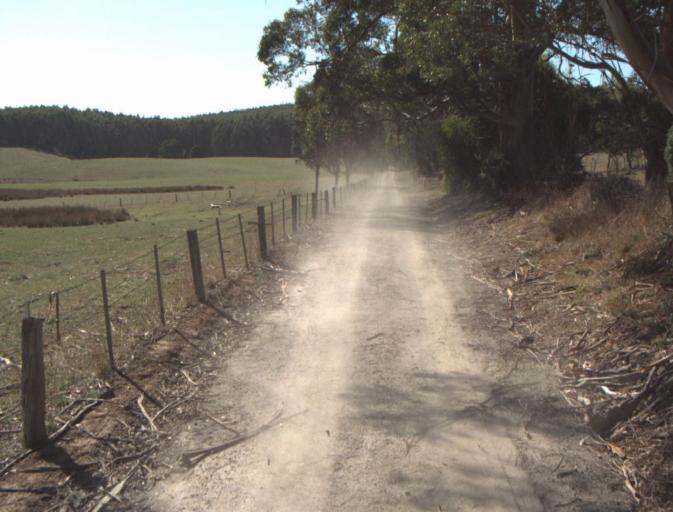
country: AU
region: Tasmania
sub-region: Launceston
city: Mayfield
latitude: -41.2209
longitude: 147.2390
